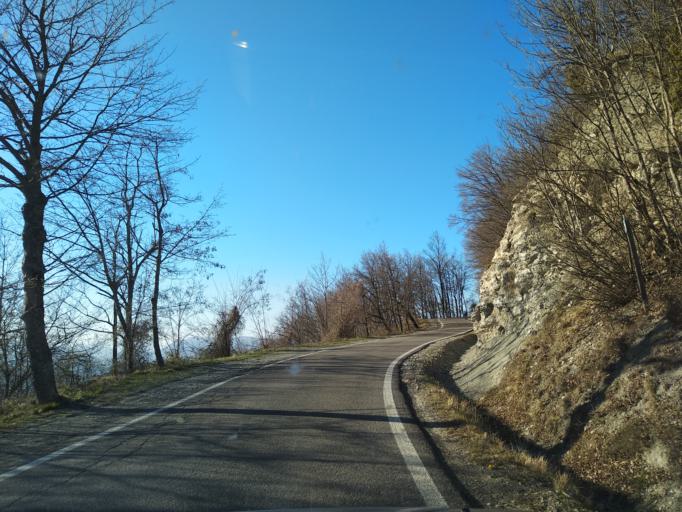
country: IT
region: Emilia-Romagna
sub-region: Provincia di Reggio Emilia
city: Castelnovo ne'Monti
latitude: 44.4181
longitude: 10.4073
